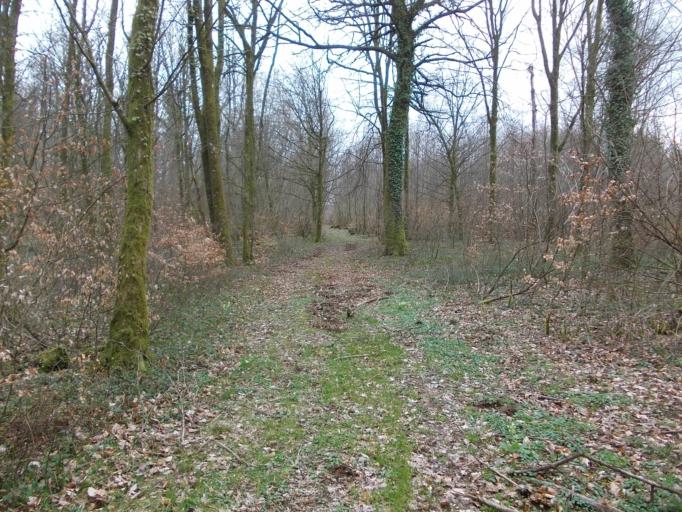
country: FR
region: Lorraine
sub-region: Departement de la Meuse
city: Ligny-en-Barrois
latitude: 48.5709
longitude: 5.3765
